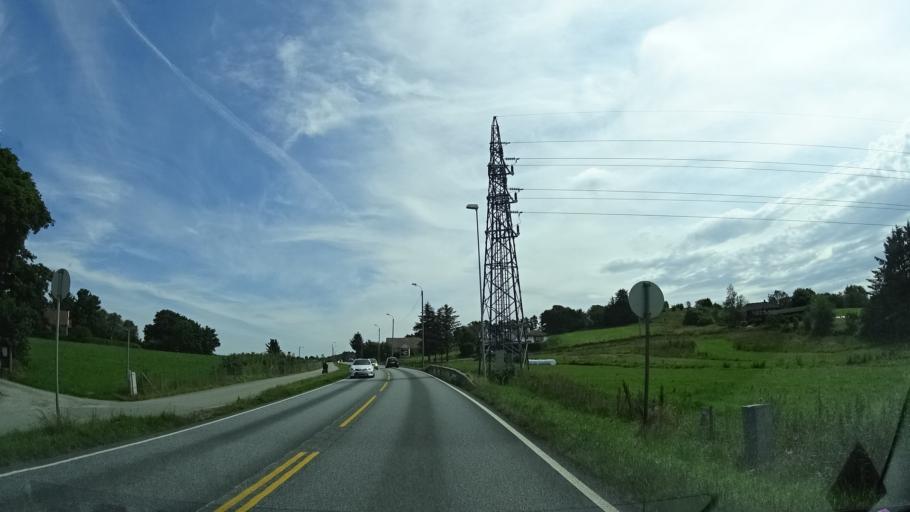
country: NO
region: Rogaland
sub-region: Randaberg
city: Randaberg
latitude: 58.9900
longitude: 5.6566
